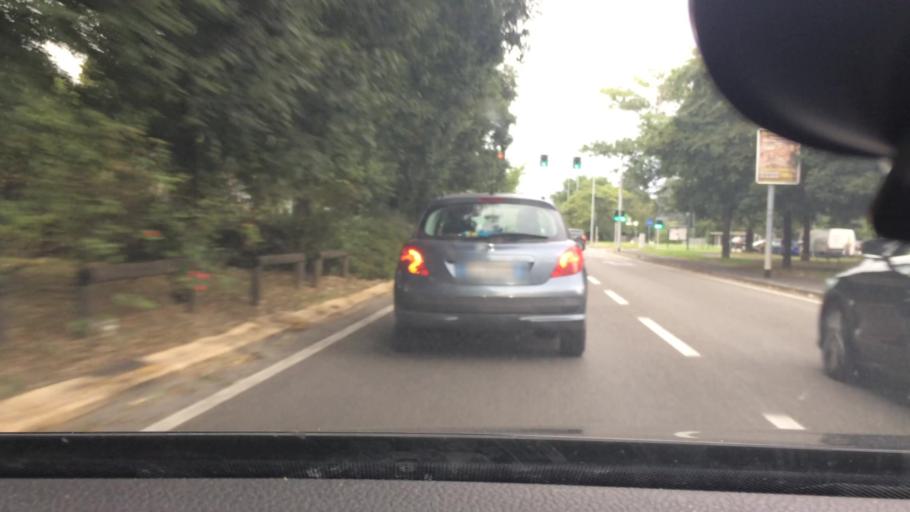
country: IT
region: Lombardy
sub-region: Citta metropolitana di Milano
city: Cinisello Balsamo
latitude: 45.5509
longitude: 9.2033
